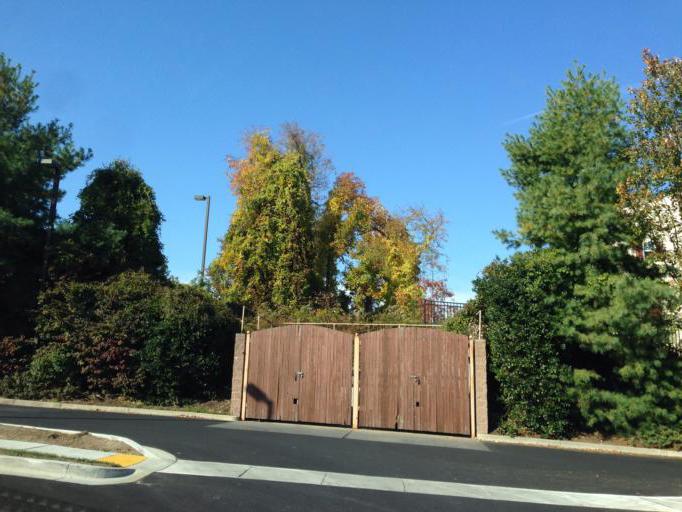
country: US
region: Maryland
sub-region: Howard County
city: Ellicott City
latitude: 39.2787
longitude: -76.8119
